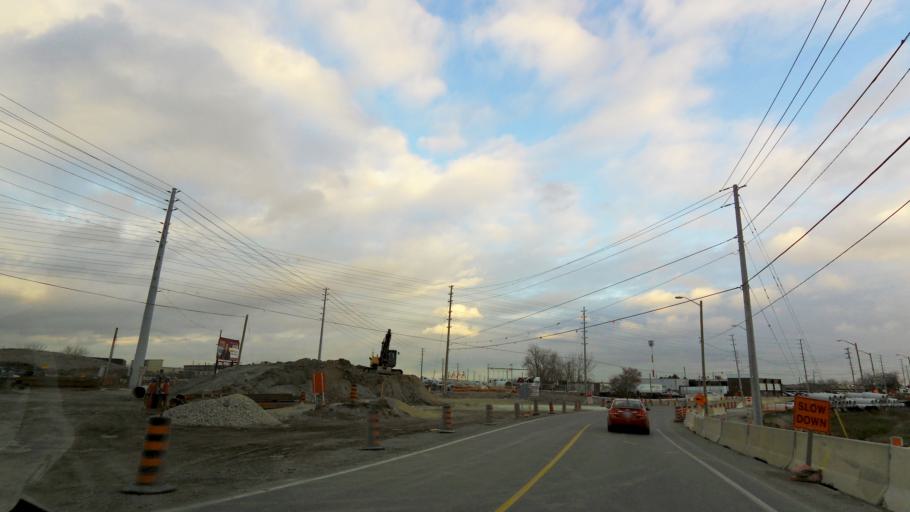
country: CA
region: Ontario
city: Brampton
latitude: 43.7038
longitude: -79.6663
